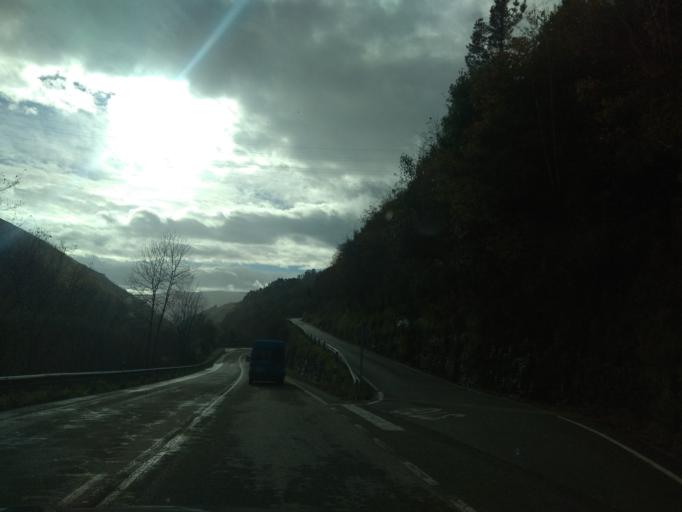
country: ES
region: Cantabria
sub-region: Provincia de Cantabria
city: San Pedro del Romeral
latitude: 43.1499
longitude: -3.8980
